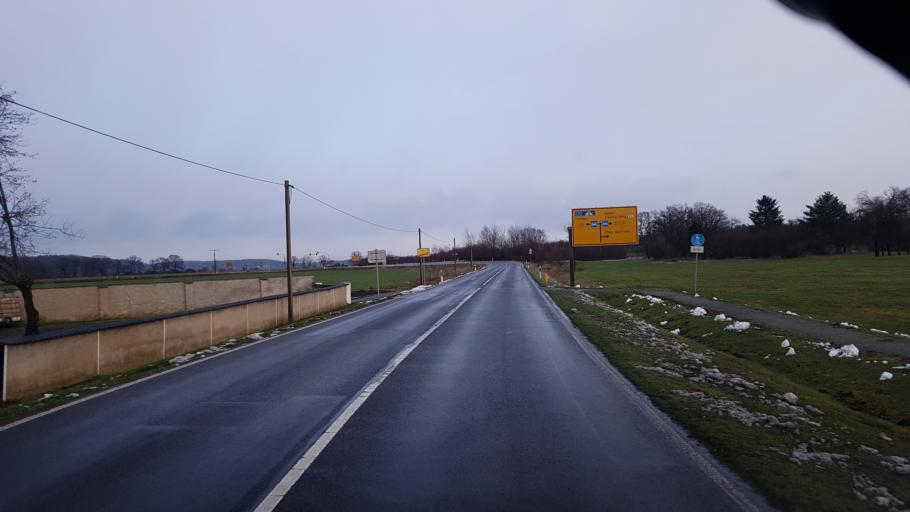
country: DE
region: Brandenburg
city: Schenkendobern
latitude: 51.8895
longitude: 14.6565
